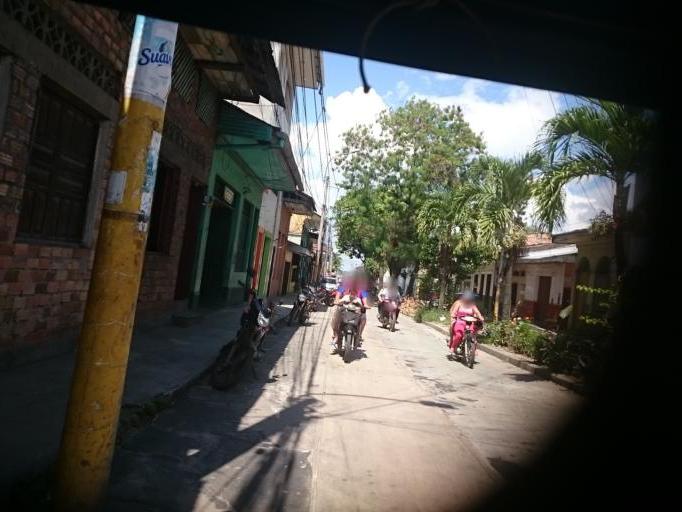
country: PE
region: Loreto
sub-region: Provincia de Maynas
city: Iquitos
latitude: -3.7458
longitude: -73.2437
